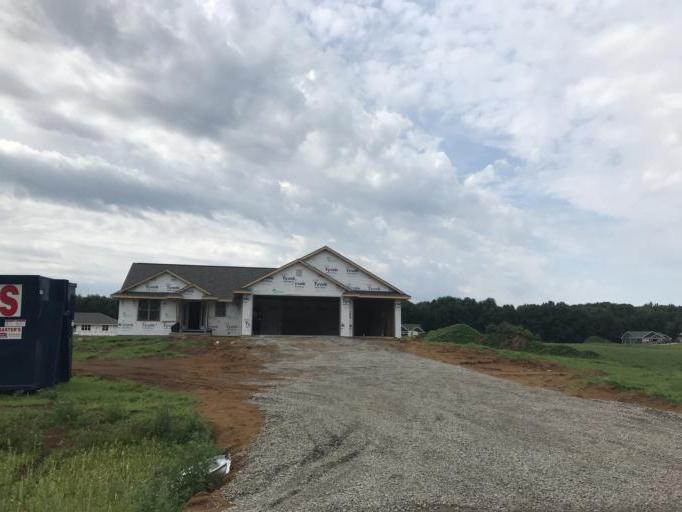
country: US
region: Wisconsin
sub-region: Brown County
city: Suamico
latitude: 44.6871
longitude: -88.0979
